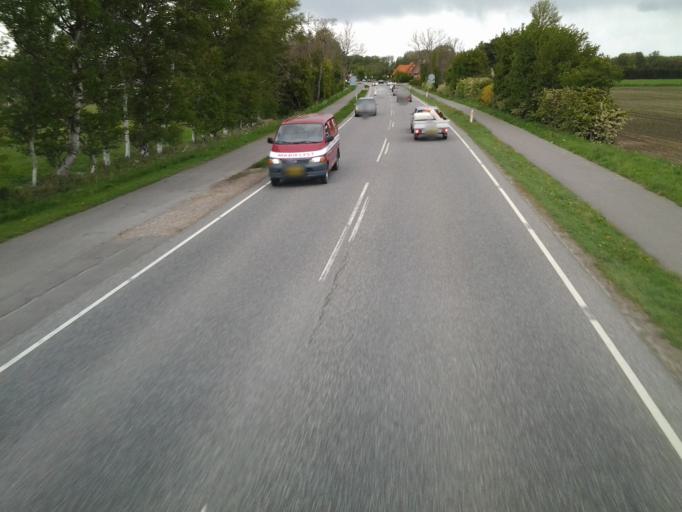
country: DK
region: Zealand
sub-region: Guldborgsund Kommune
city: Nykobing Falster
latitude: 54.7312
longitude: 11.9229
